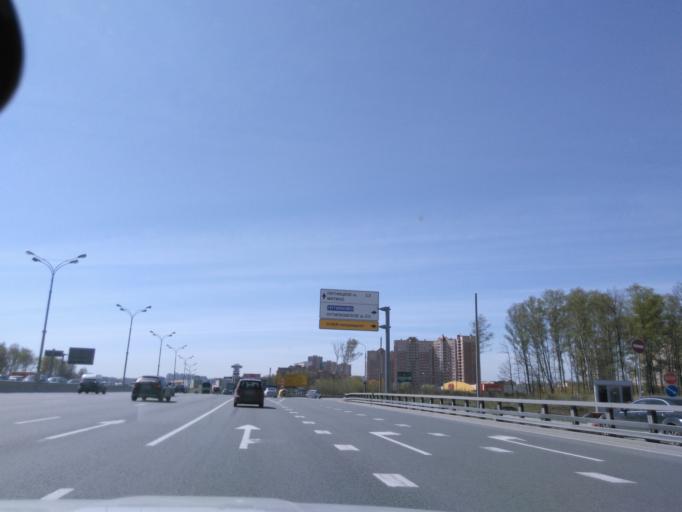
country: RU
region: Moscow
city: Khimki
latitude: 55.8661
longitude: 37.4038
